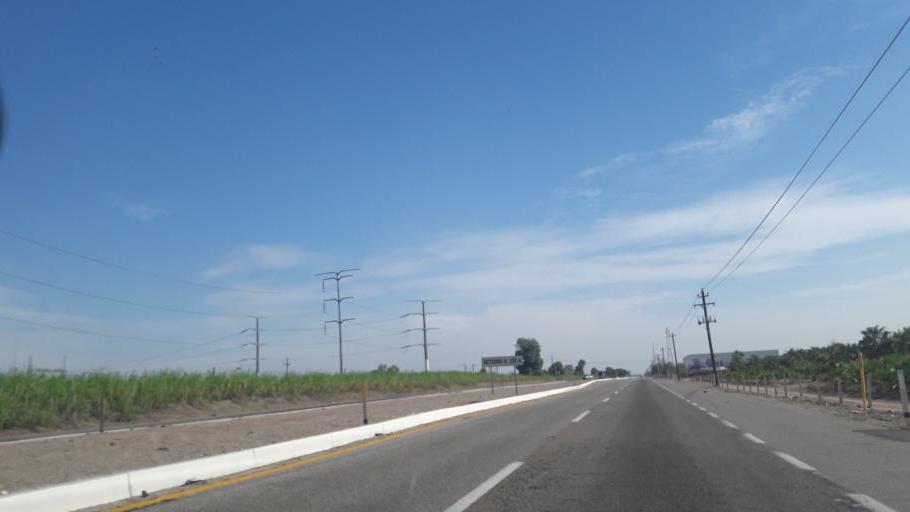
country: MX
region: Baja California
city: Progreso
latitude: 32.5954
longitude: -115.6328
